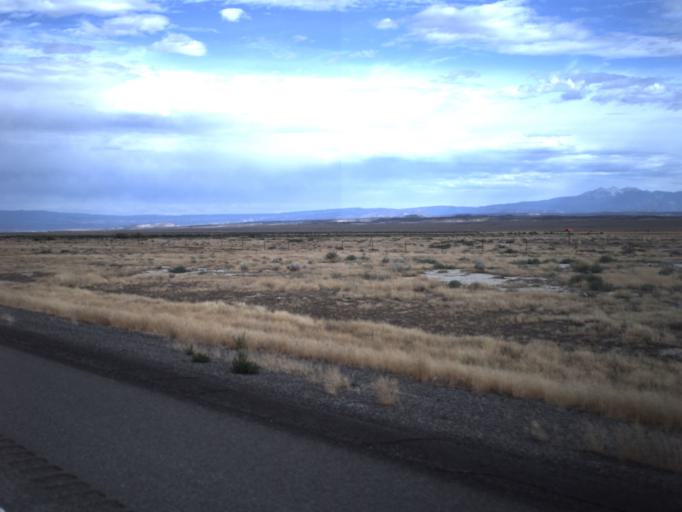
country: US
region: Utah
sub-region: Grand County
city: Moab
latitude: 38.9418
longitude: -109.5983
